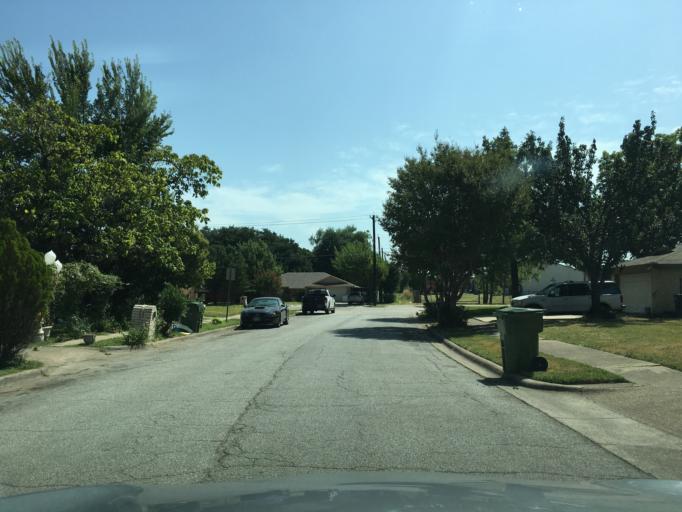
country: US
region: Texas
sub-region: Dallas County
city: Garland
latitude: 32.8837
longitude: -96.6229
